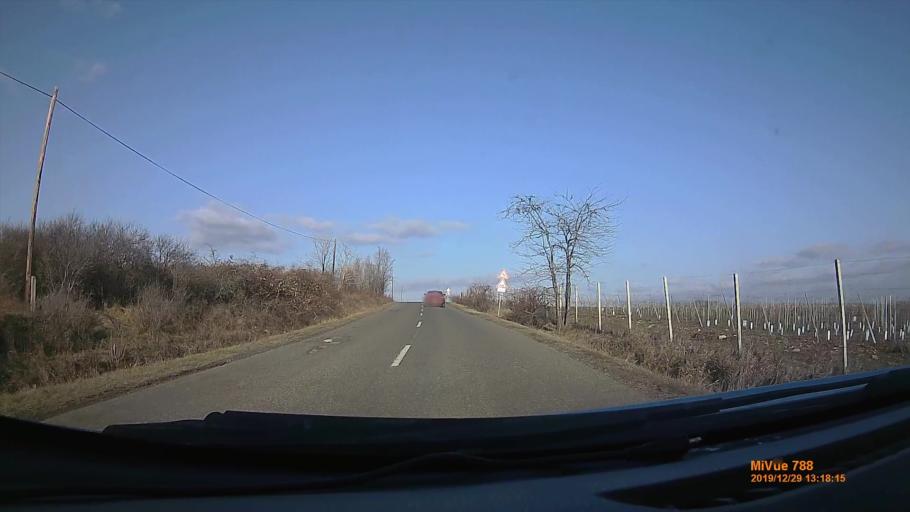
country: HU
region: Heves
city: Domoszlo
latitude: 47.8347
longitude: 20.1293
